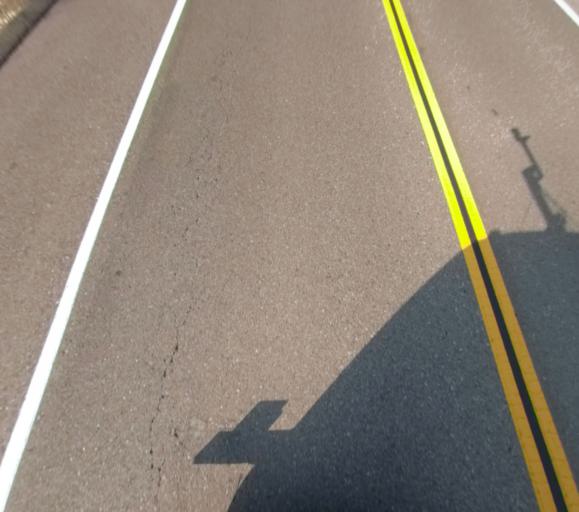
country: US
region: California
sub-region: Madera County
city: Coarsegold
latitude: 37.1574
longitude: -119.6465
